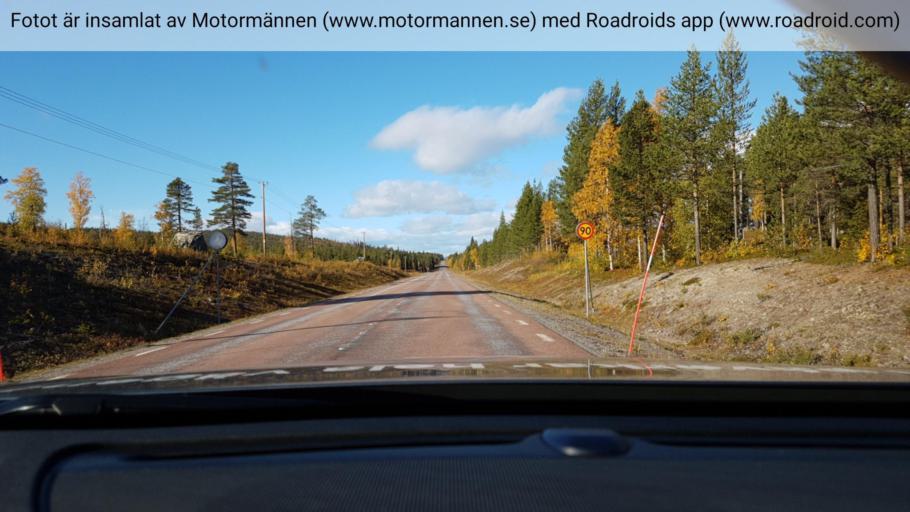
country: SE
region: Norrbotten
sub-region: Arjeplogs Kommun
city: Arjeplog
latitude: 66.0524
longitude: 18.0116
